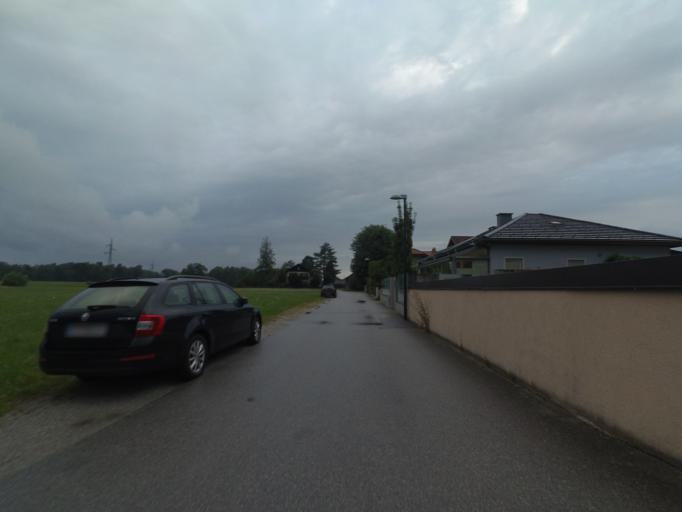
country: AT
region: Salzburg
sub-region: Politischer Bezirk Salzburg-Umgebung
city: Grodig
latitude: 47.7561
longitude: 13.0333
